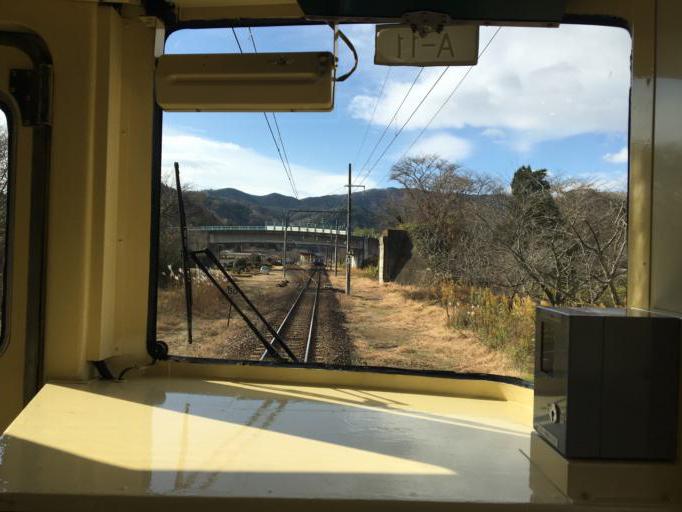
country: JP
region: Miyagi
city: Marumori
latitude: 37.9322
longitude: 140.7641
